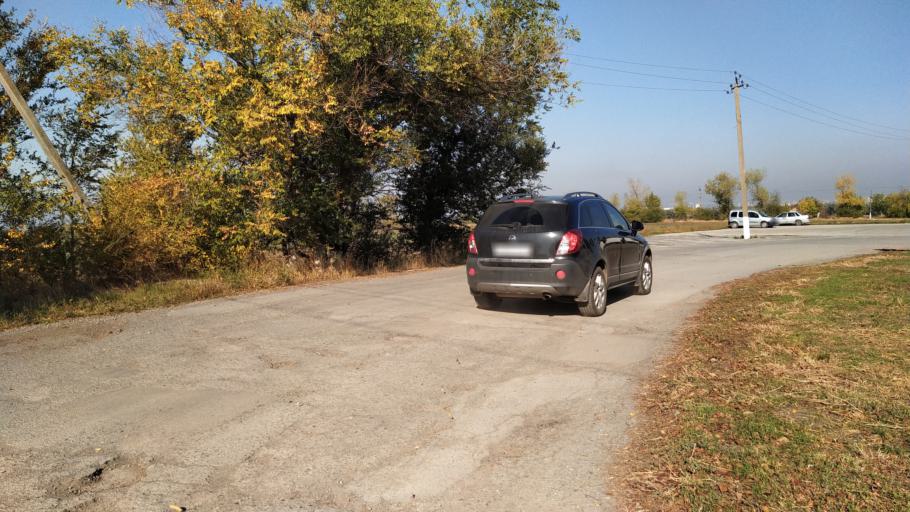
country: RU
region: Rostov
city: Bataysk
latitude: 47.0875
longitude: 39.7774
